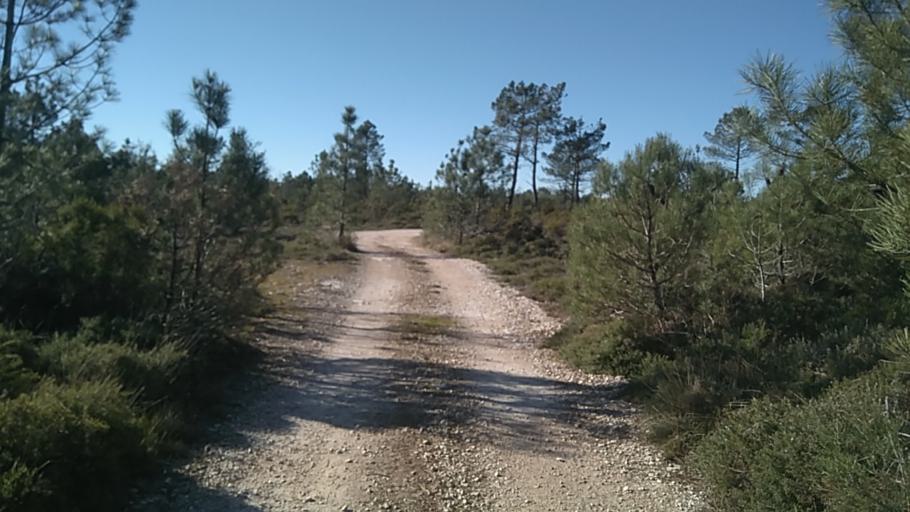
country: PT
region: Leiria
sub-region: Alcobaca
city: Aljubarrota
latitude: 39.5386
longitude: -8.8658
